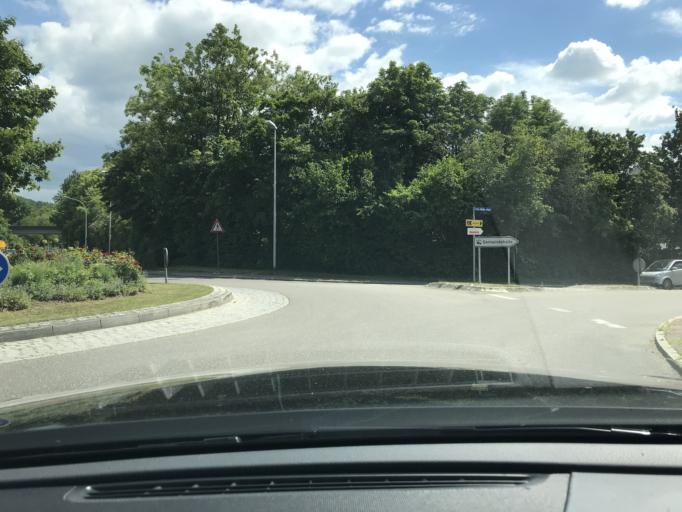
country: DE
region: Baden-Wuerttemberg
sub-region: Regierungsbezirk Stuttgart
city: Schwaikheim
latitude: 48.8712
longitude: 9.3595
